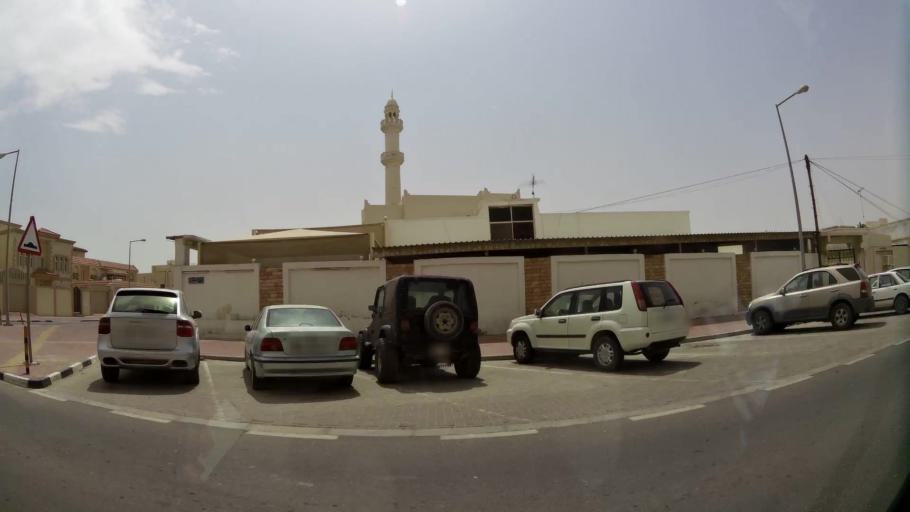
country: QA
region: Baladiyat ar Rayyan
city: Ar Rayyan
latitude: 25.3152
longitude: 51.4748
